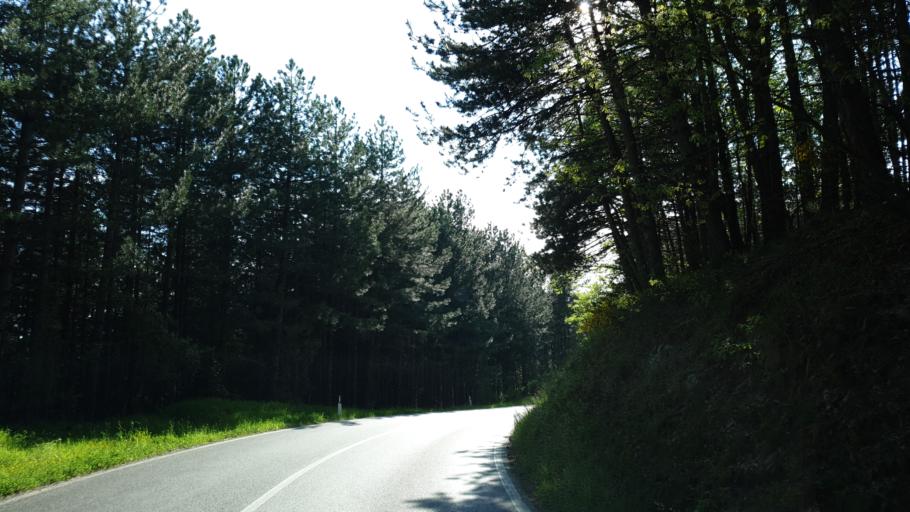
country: IT
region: Tuscany
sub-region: Province of Arezzo
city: Montemignaio
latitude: 43.7879
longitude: 11.6360
